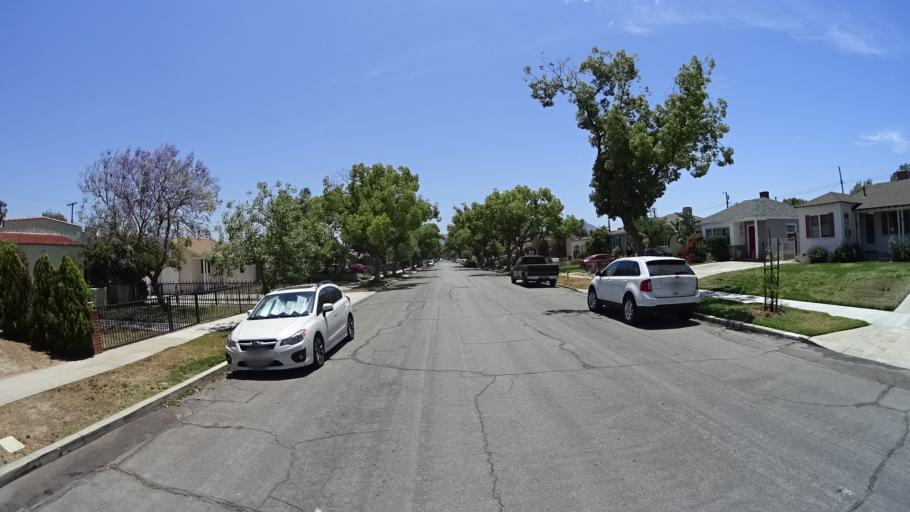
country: US
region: California
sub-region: Los Angeles County
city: Burbank
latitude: 34.1782
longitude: -118.3354
